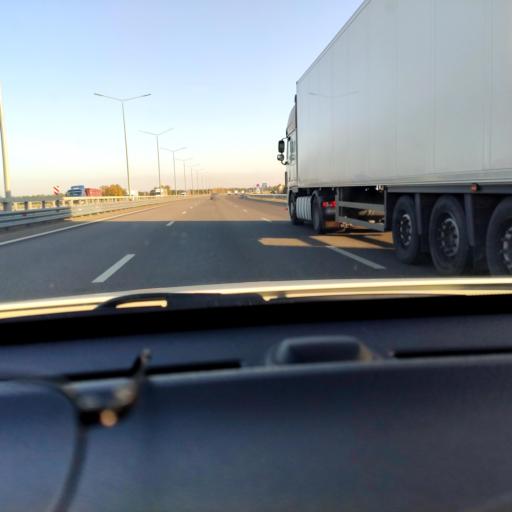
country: RU
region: Voronezj
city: Somovo
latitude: 51.7892
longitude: 39.2787
